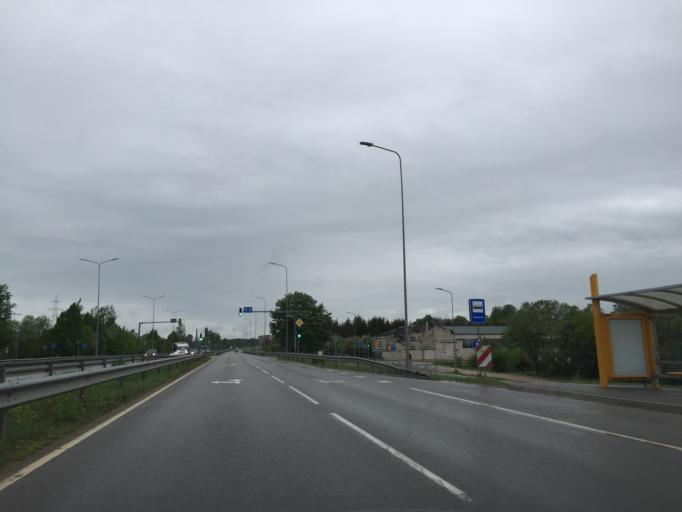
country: LV
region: Ogre
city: Ogre
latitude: 56.8044
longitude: 24.6108
